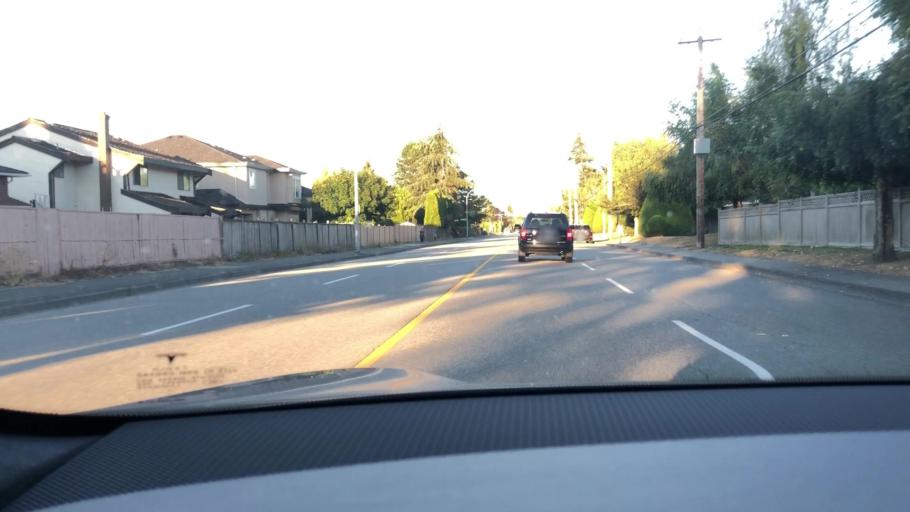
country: CA
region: British Columbia
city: Richmond
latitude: 49.1484
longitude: -123.1743
